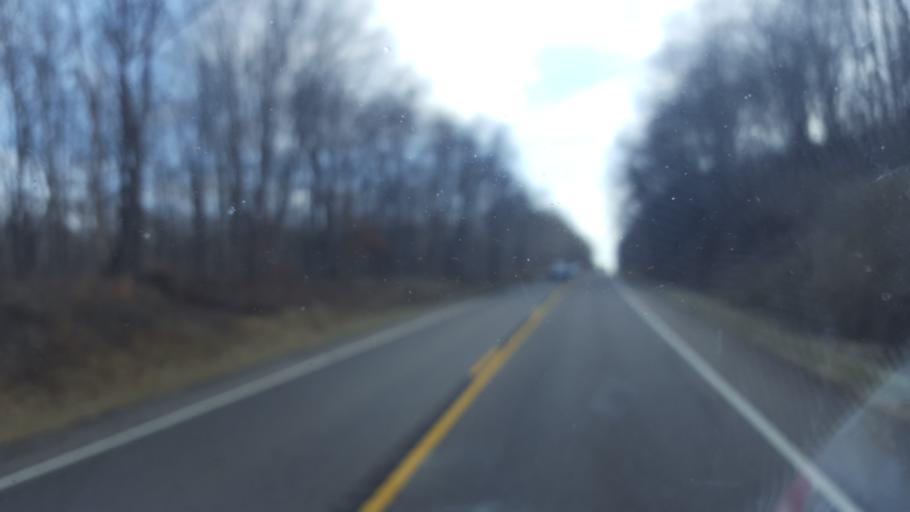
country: US
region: Ohio
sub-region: Stark County
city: East Canton
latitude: 40.7693
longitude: -81.2189
